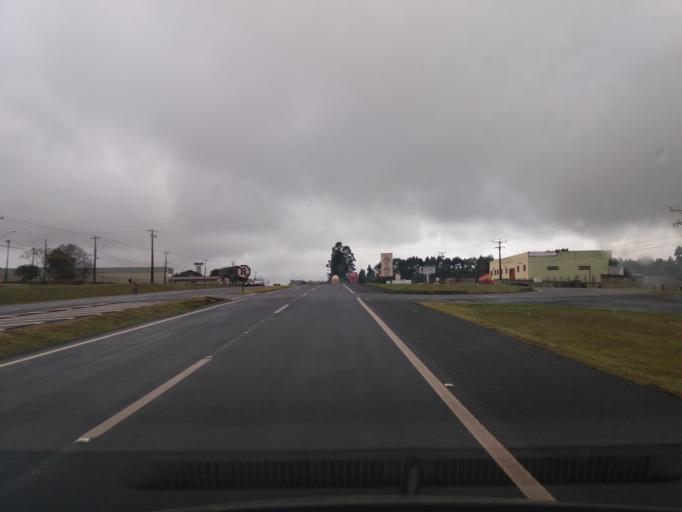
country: BR
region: Parana
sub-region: Cascavel
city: Cascavel
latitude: -24.9976
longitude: -53.5168
